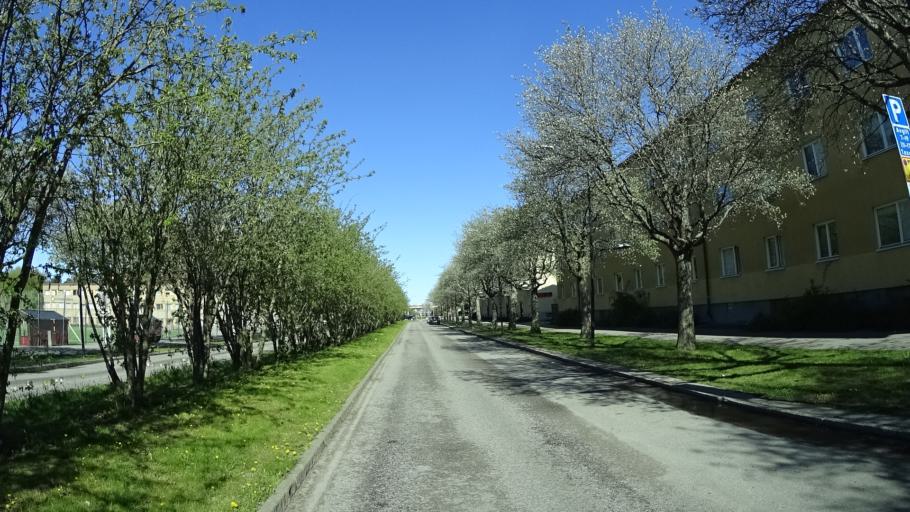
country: SE
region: Stockholm
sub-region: Stockholms Kommun
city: Arsta
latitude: 59.2826
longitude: 18.0754
